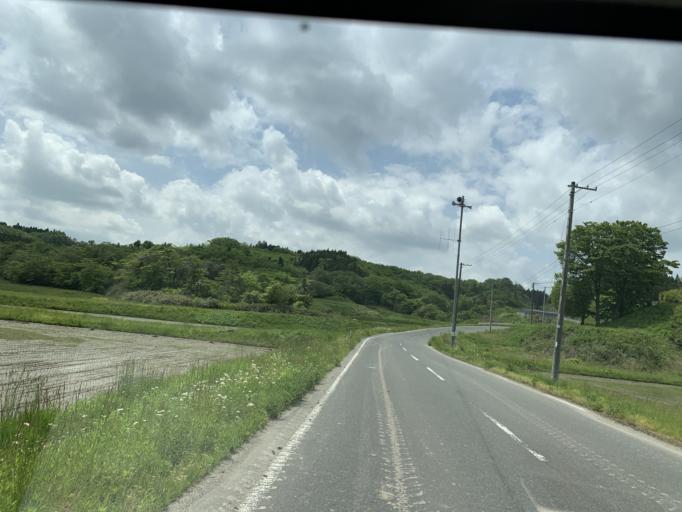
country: JP
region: Miyagi
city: Furukawa
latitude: 38.7250
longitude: 140.9256
